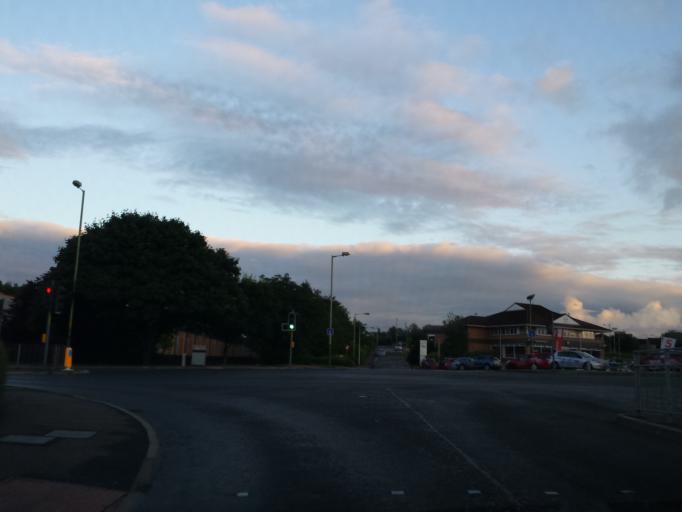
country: GB
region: Scotland
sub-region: Perth and Kinross
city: Luncarty
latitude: 56.4074
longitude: -3.4806
